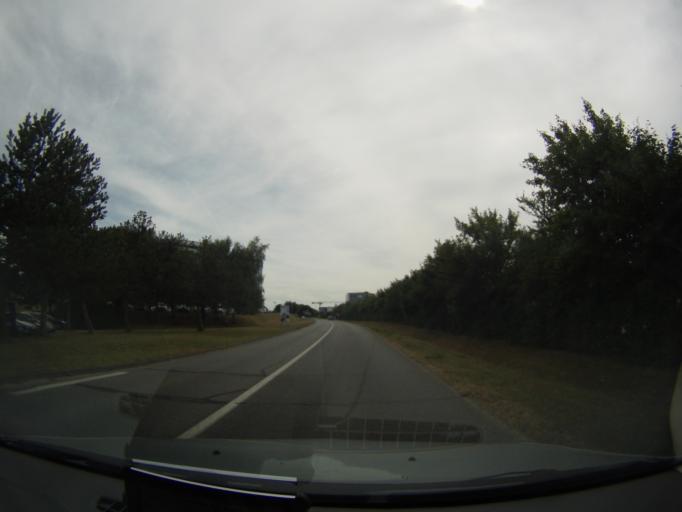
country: FR
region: Poitou-Charentes
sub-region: Departement de la Vienne
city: Jaunay-Clan
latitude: 46.6712
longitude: 0.3623
